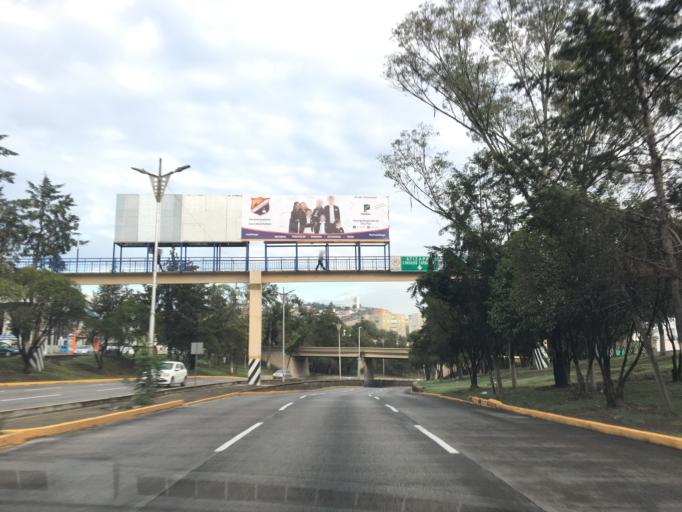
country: MX
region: Mexico
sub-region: Naucalpan de Juarez
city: Ejido del Tejocote
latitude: 19.5076
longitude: -99.2597
